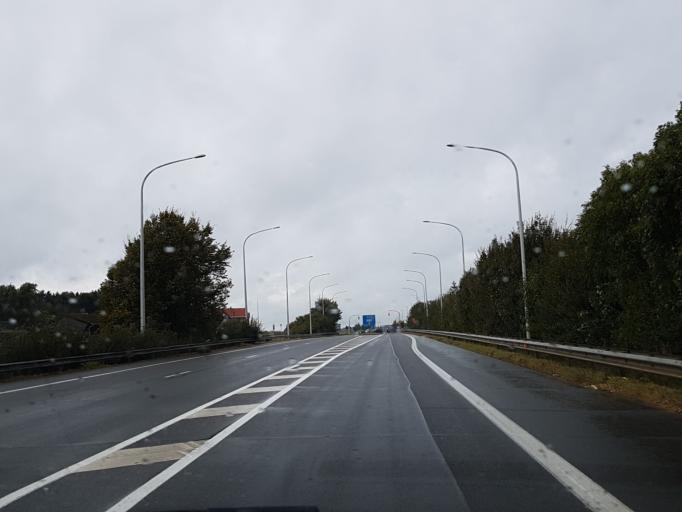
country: BE
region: Flanders
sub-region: Provincie Vlaams-Brabant
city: Tienen
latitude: 50.7968
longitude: 4.9255
